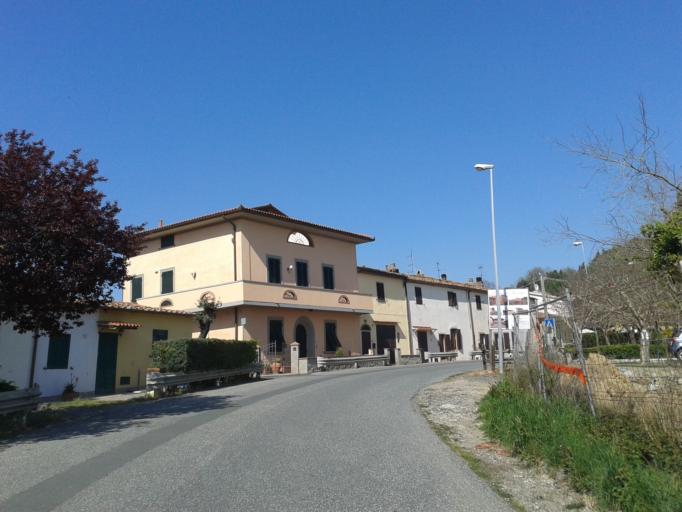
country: IT
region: Tuscany
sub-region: Provincia di Livorno
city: Quercianella
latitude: 43.4621
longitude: 10.4108
